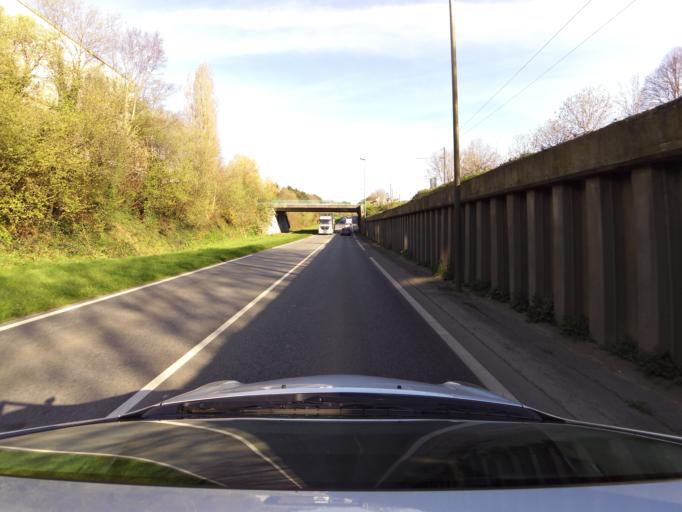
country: FR
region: Brittany
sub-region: Departement du Morbihan
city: Lorient
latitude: 47.7420
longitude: -3.3834
